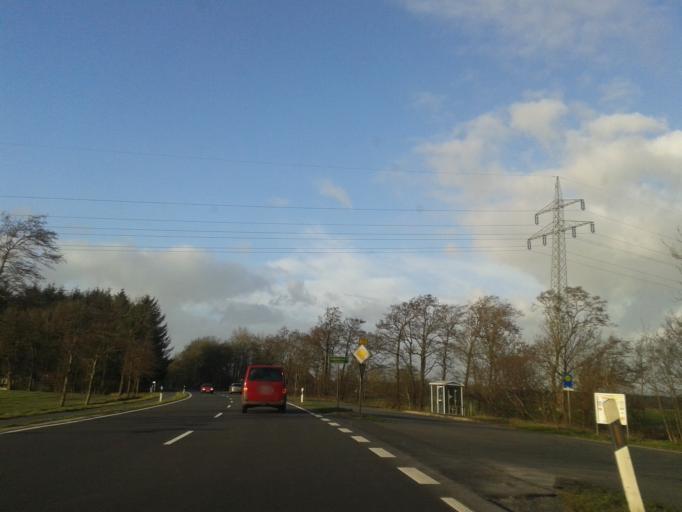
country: DE
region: Lower Saxony
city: Osteel
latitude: 53.5561
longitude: 7.2539
